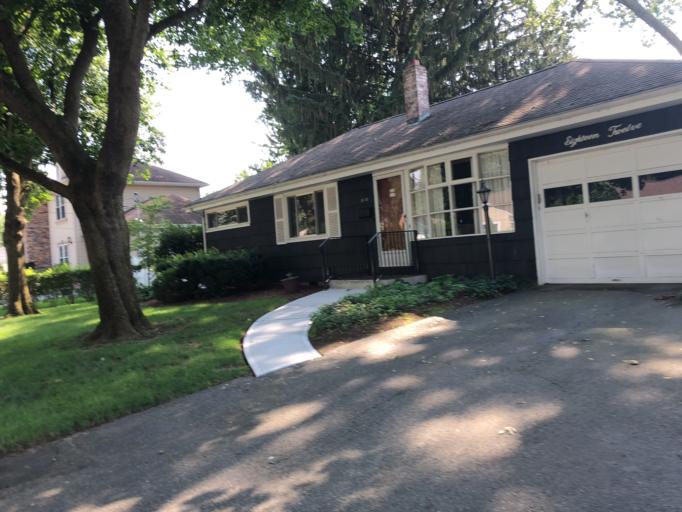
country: US
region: New Jersey
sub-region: Bergen County
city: Fair Lawn
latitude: 40.9470
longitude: -74.1086
